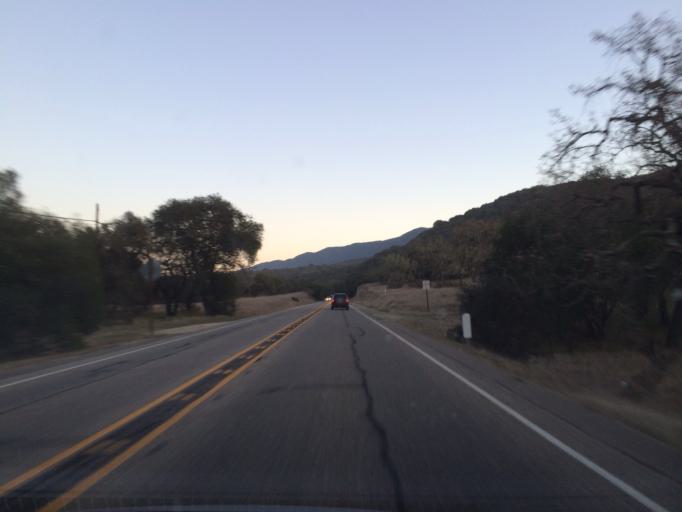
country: US
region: California
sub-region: Santa Barbara County
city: Santa Ynez
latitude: 34.5827
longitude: -119.9913
